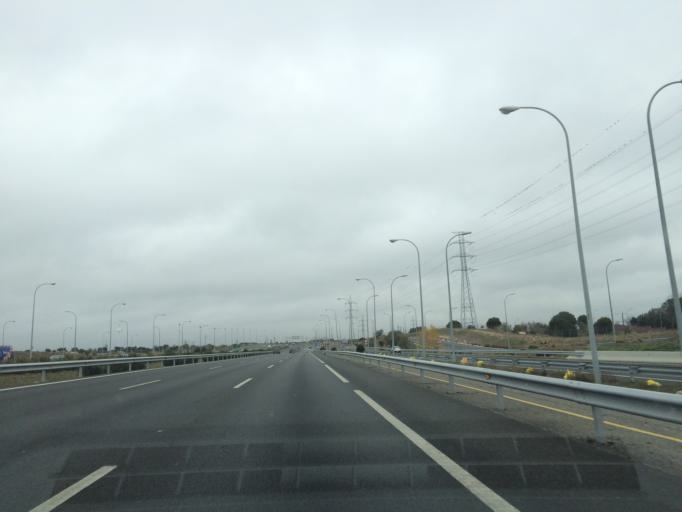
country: ES
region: Madrid
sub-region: Provincia de Madrid
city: Pozuelo de Alarcon
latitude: 40.4010
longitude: -3.8317
